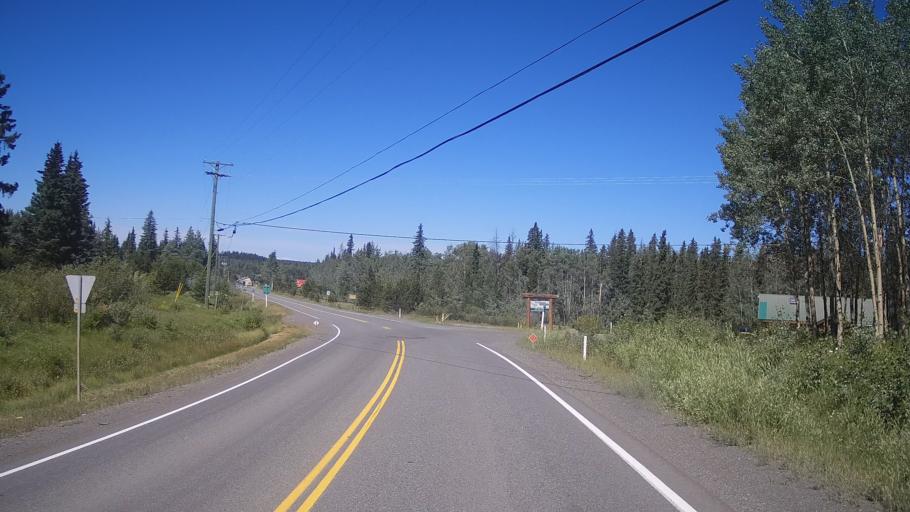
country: CA
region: British Columbia
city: Cache Creek
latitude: 51.5541
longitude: -121.1943
